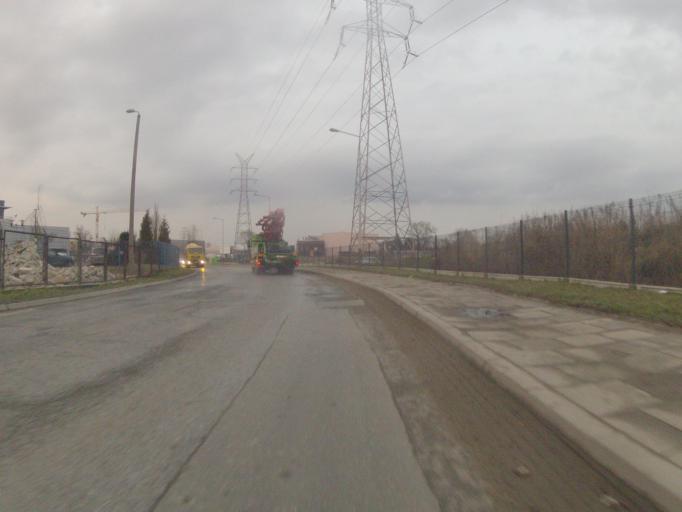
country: PL
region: Lesser Poland Voivodeship
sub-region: Powiat wielicki
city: Czarnochowice
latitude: 50.0519
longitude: 20.0164
